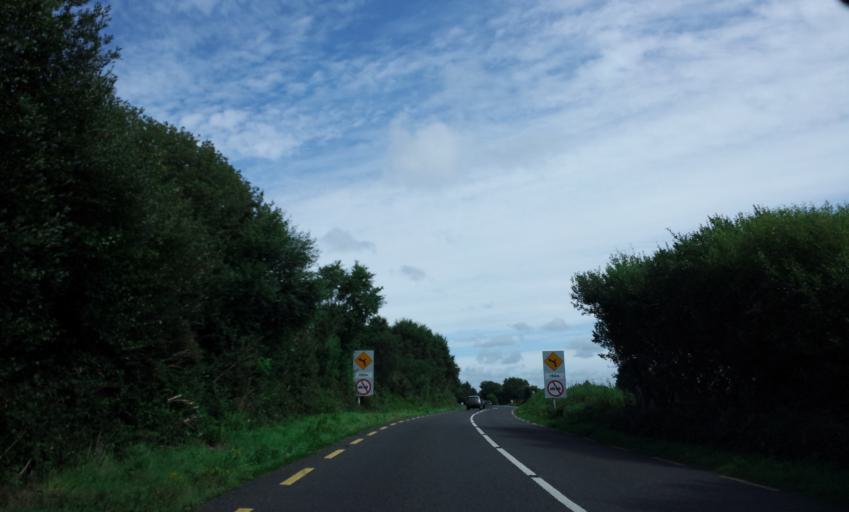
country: IE
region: Munster
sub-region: Ciarrai
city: Killorglin
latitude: 52.0705
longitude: -9.8861
